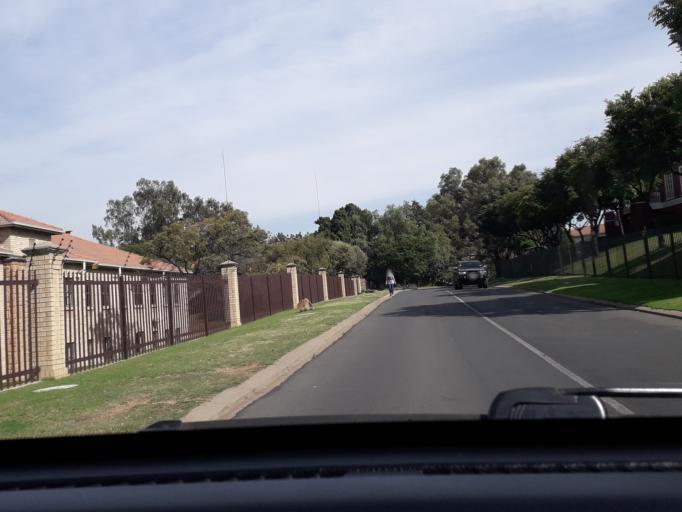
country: ZA
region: Gauteng
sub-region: City of Johannesburg Metropolitan Municipality
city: Diepsloot
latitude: -26.0449
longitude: 28.0111
